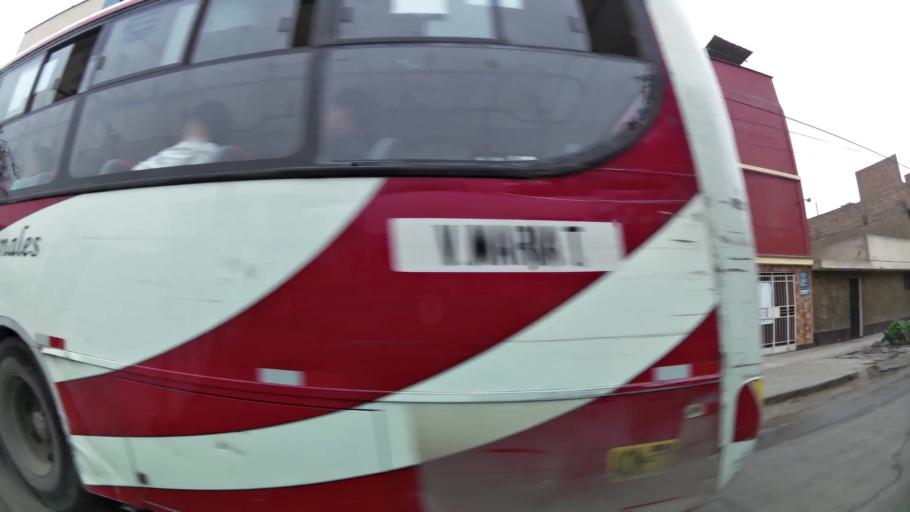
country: PE
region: Lima
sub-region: Lima
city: Urb. Santo Domingo
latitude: -11.9017
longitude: -77.0358
